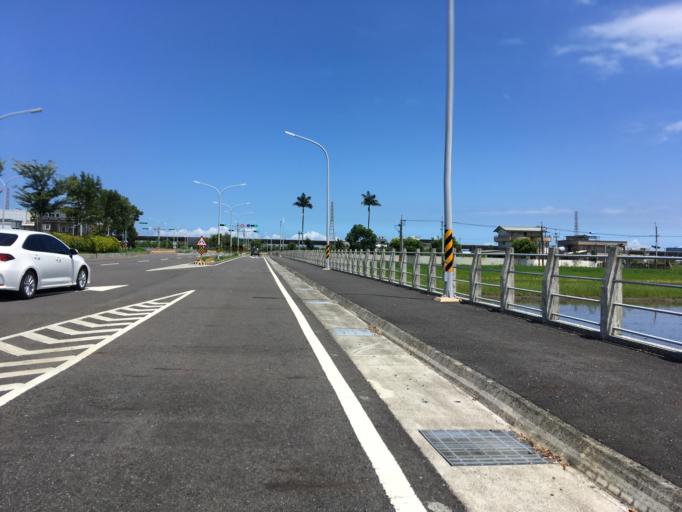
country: TW
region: Taiwan
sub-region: Yilan
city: Yilan
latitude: 24.6934
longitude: 121.7854
